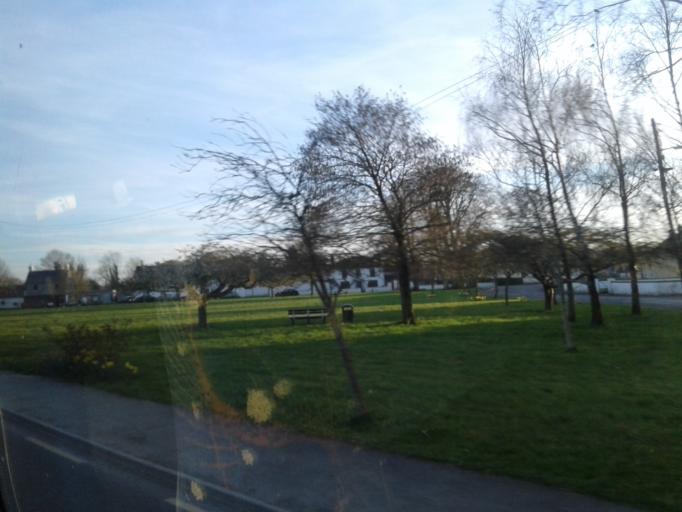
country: IE
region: Leinster
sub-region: Uibh Fhaili
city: Daingean
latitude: 53.2318
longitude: -7.3063
